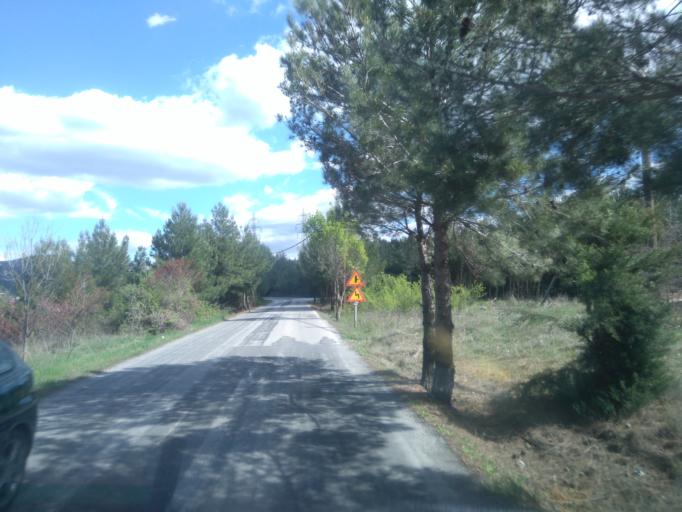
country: GR
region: Central Macedonia
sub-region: Nomos Thessalonikis
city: Asvestochori
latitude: 40.6415
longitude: 23.0060
